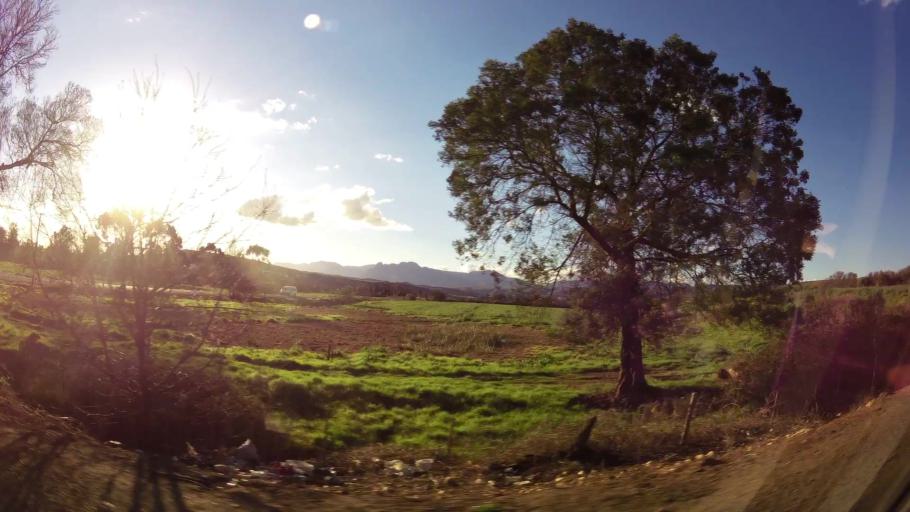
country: ZA
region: Western Cape
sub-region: Eden District Municipality
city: Riversdale
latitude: -34.0921
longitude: 20.9675
